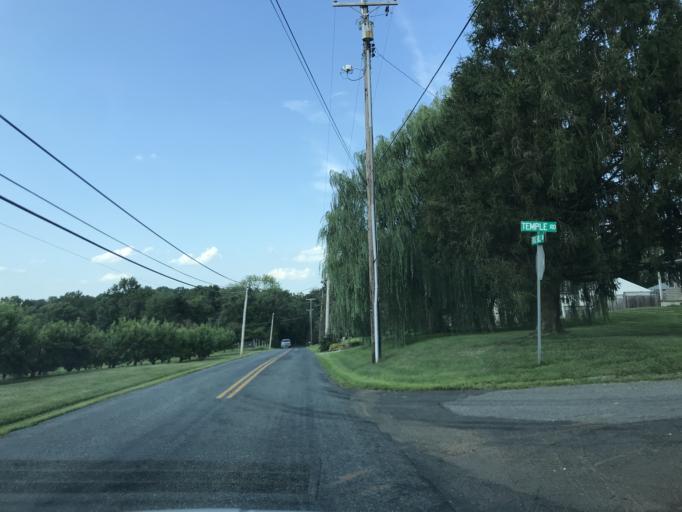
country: US
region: Maryland
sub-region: Harford County
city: South Bel Air
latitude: 39.6081
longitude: -76.2995
